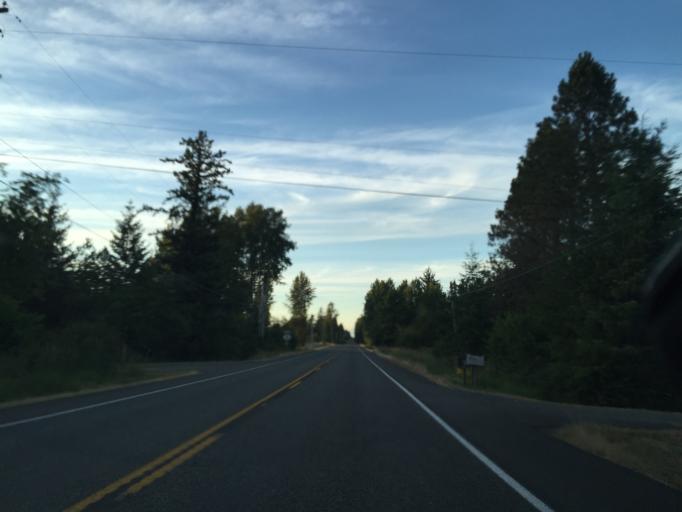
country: US
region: Washington
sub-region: Whatcom County
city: Geneva
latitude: 48.8193
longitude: -122.3770
